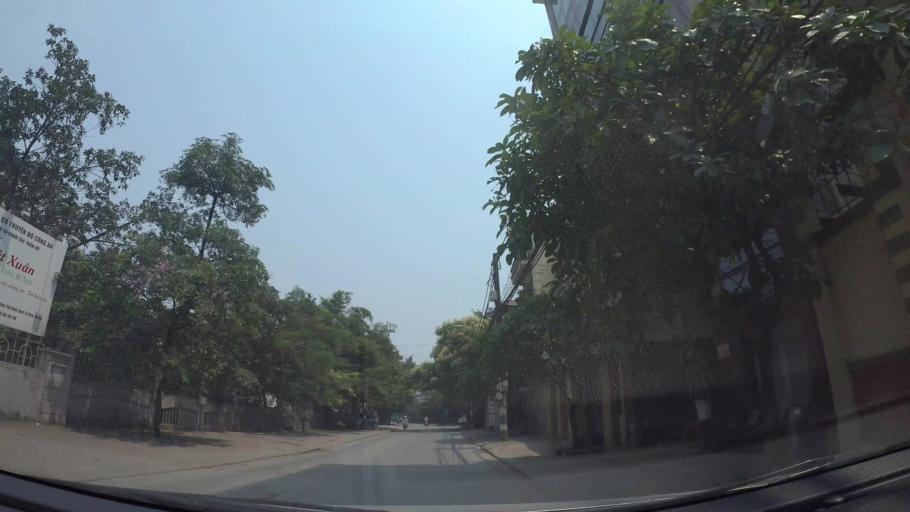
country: VN
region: Ha Noi
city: Thanh Xuan
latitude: 20.9957
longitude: 105.7891
